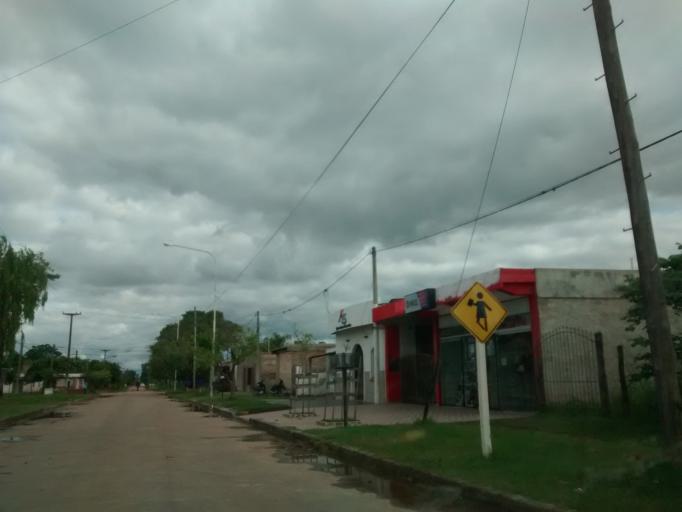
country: AR
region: Chaco
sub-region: Departamento de Quitilipi
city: Quitilipi
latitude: -26.8746
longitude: -60.2186
